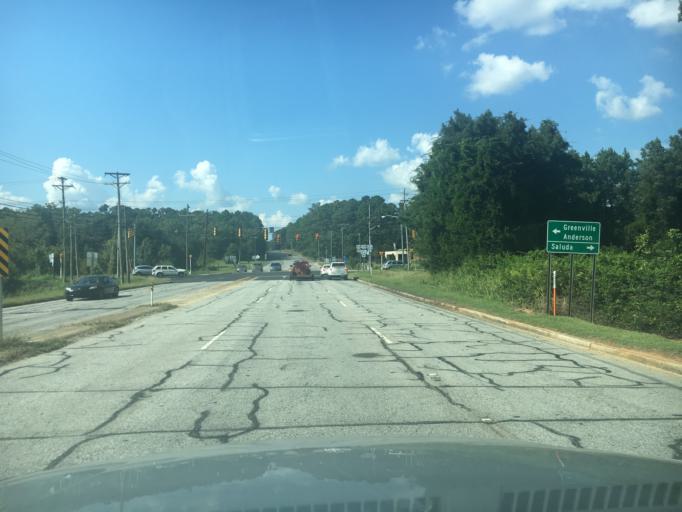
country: US
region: South Carolina
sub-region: Greenwood County
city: Greenwood
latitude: 34.2157
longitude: -82.1681
